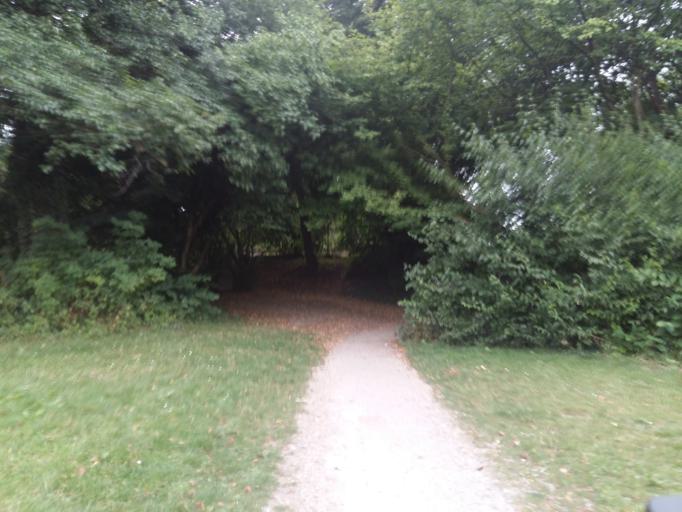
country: FR
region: Picardie
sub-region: Departement de la Somme
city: Amiens
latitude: 49.8984
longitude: 2.2719
